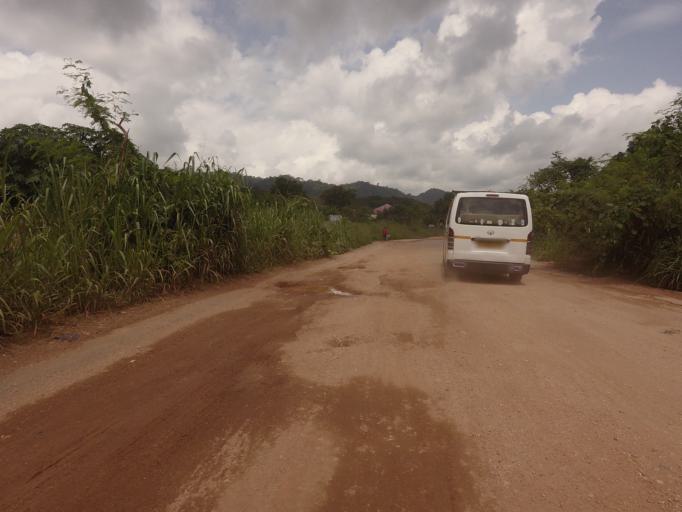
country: GH
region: Volta
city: Ho
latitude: 6.6935
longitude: 0.3359
